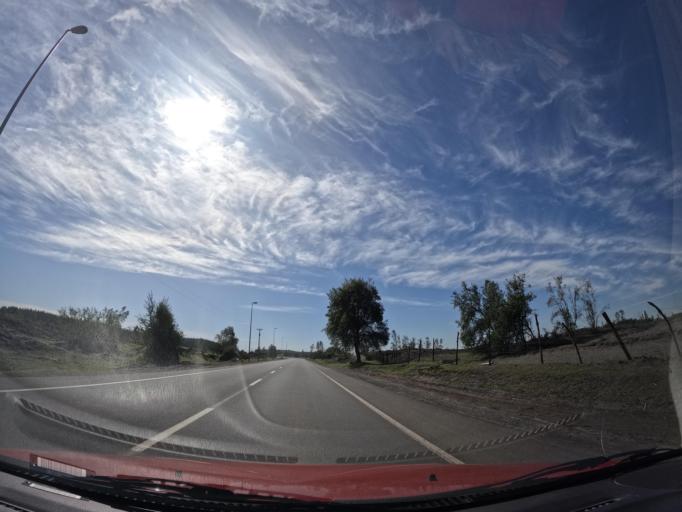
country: CL
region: Biobio
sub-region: Provincia de Biobio
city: Cabrero
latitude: -36.9363
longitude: -72.3449
